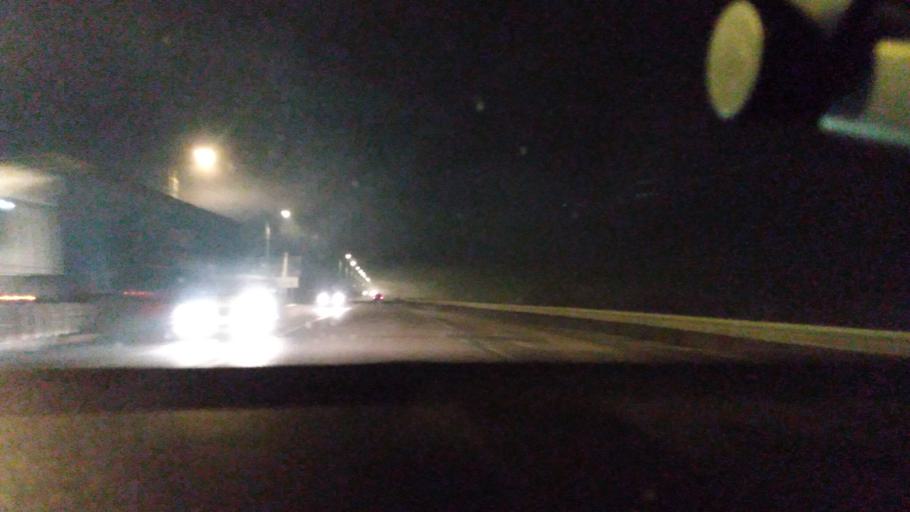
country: RU
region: Moskovskaya
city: Yegor'yevsk
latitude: 55.4392
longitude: 39.0210
